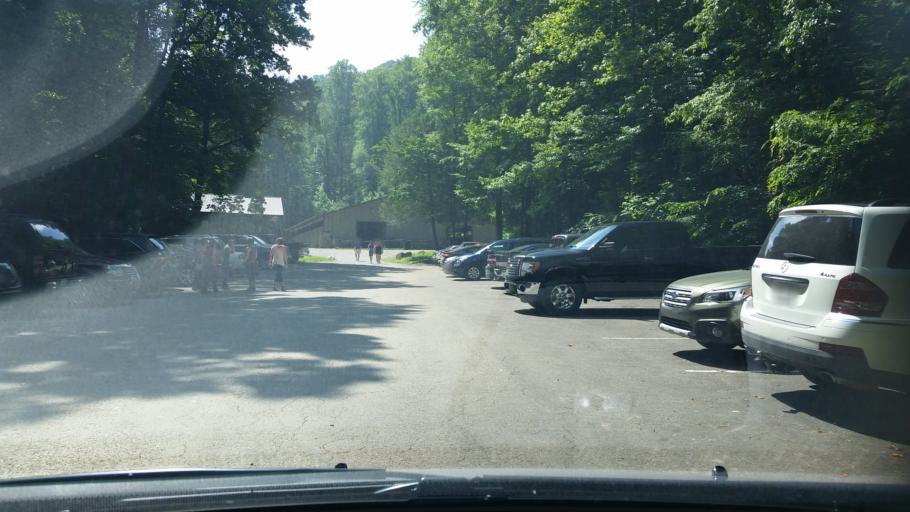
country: US
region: Tennessee
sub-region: Sevier County
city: Gatlinburg
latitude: 35.6910
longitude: -83.5323
